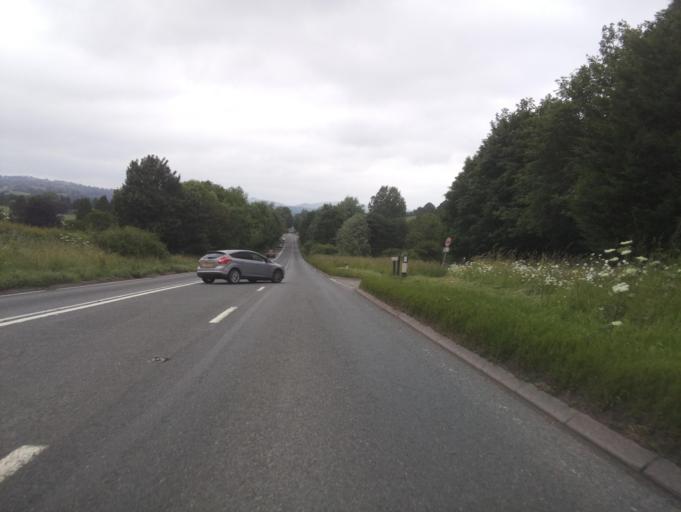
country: GB
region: England
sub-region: Staffordshire
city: Mayfield
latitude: 52.9951
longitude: -1.7491
